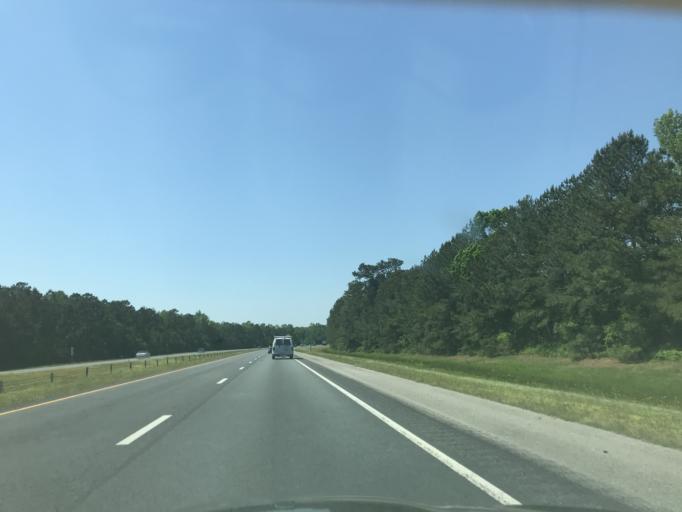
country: US
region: North Carolina
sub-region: Johnston County
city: Benson
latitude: 35.3434
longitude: -78.4702
